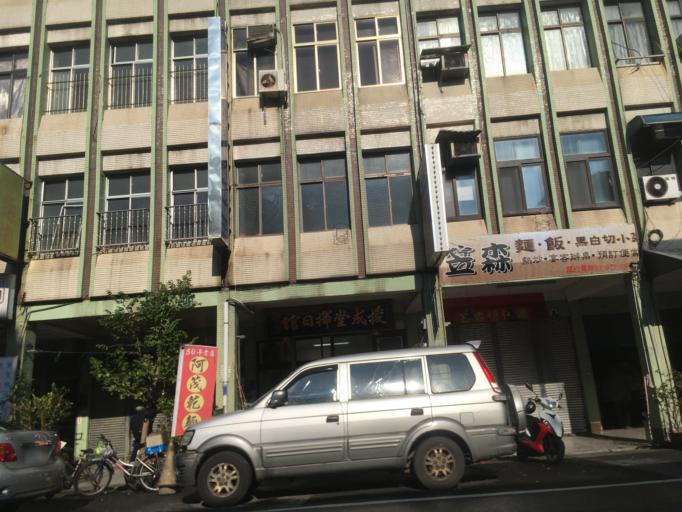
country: TW
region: Taiwan
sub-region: Yilan
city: Yilan
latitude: 24.8569
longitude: 121.8249
